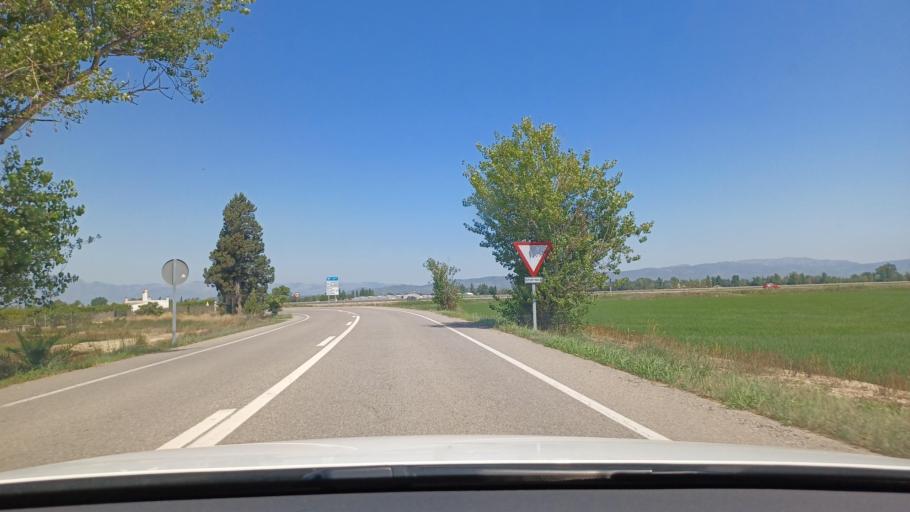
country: ES
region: Catalonia
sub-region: Provincia de Tarragona
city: Amposta
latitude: 40.7060
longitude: 0.6417
